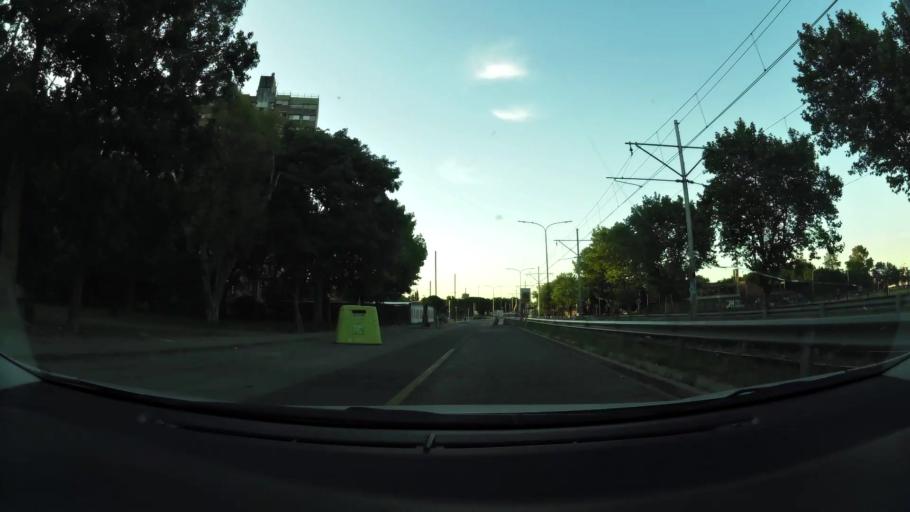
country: AR
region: Buenos Aires F.D.
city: Villa Lugano
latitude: -34.6814
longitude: -58.4645
